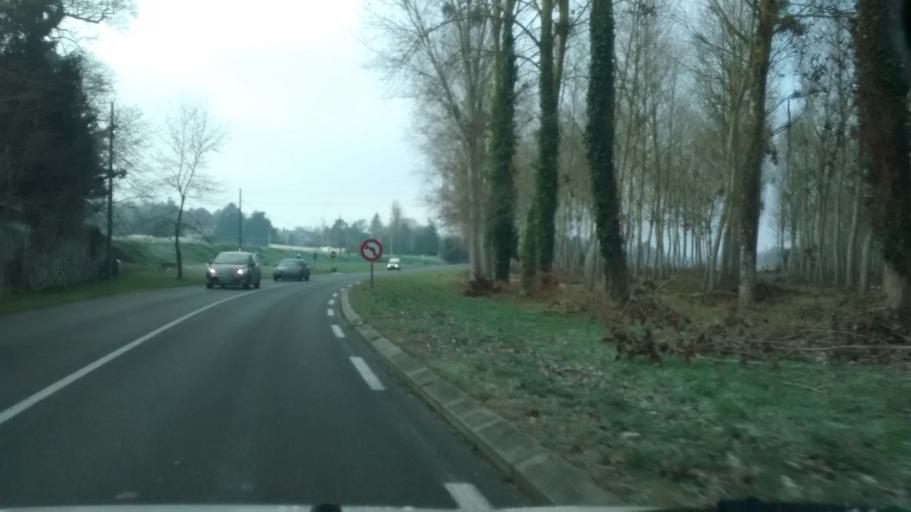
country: FR
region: Centre
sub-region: Departement d'Indre-et-Loire
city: Ballan-Mire
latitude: 47.3645
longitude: 0.6312
